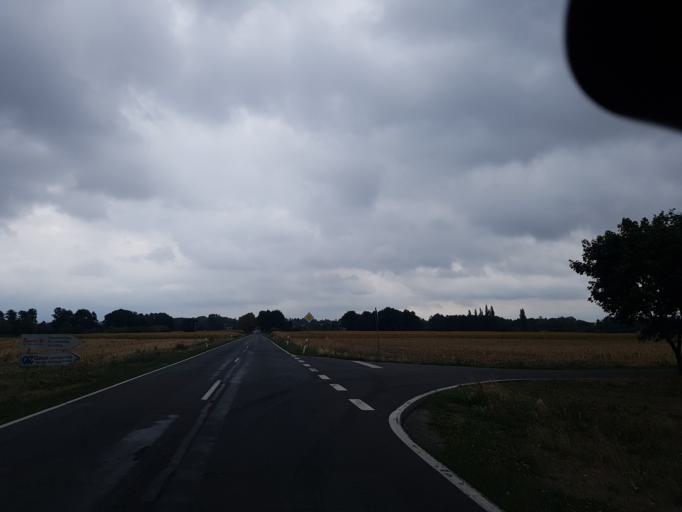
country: DE
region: Saxony-Anhalt
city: Loburg
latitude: 52.1249
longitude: 12.0900
